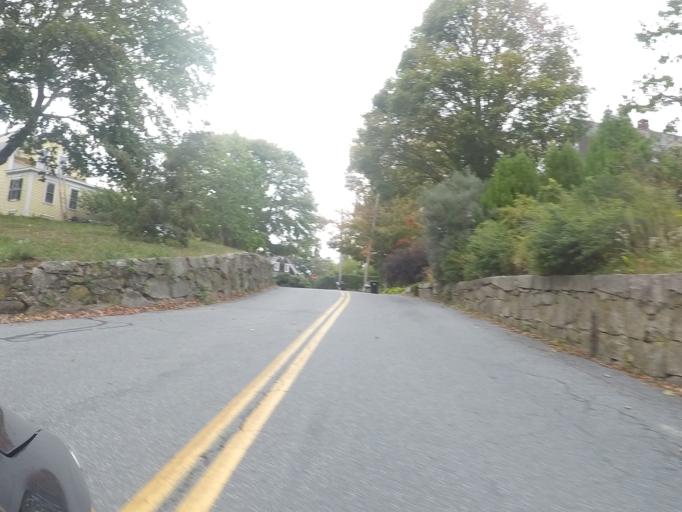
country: US
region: Massachusetts
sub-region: Bristol County
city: Smith Mills
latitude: 41.5715
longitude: -71.0048
